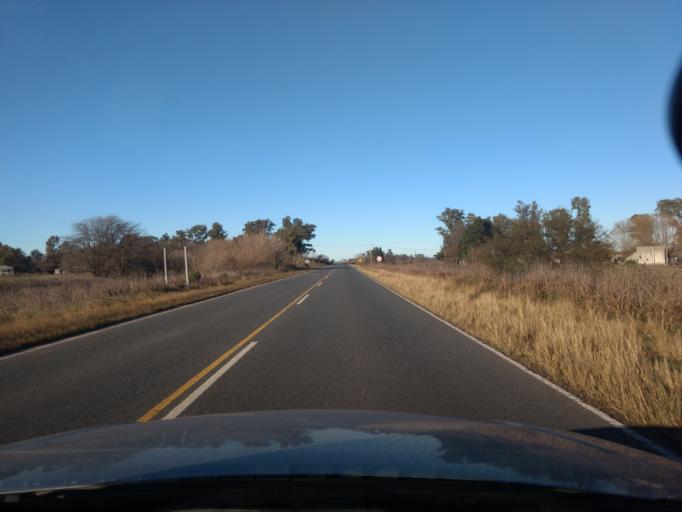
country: AR
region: Buenos Aires
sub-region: Partido de Lujan
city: Lujan
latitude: -34.6238
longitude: -59.1078
